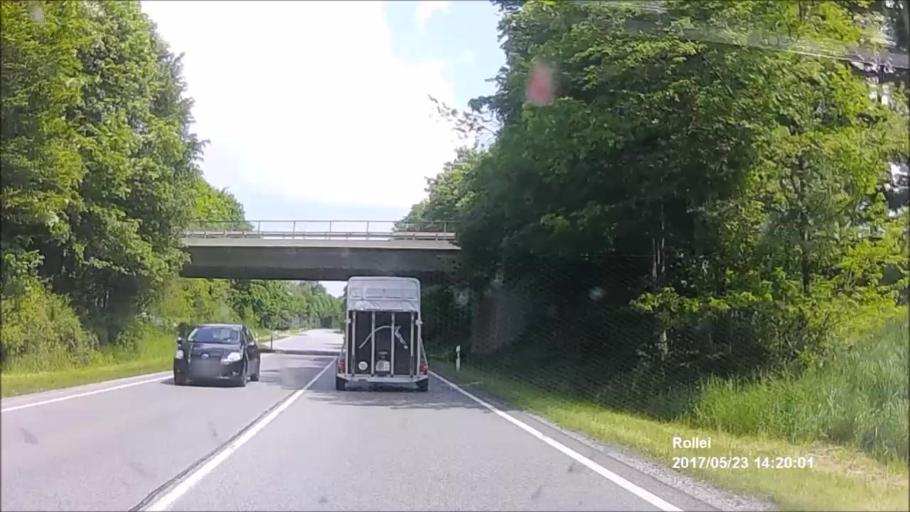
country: DE
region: Bavaria
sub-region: Upper Bavaria
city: Wasserburg am Inn
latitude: 48.0658
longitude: 12.2442
